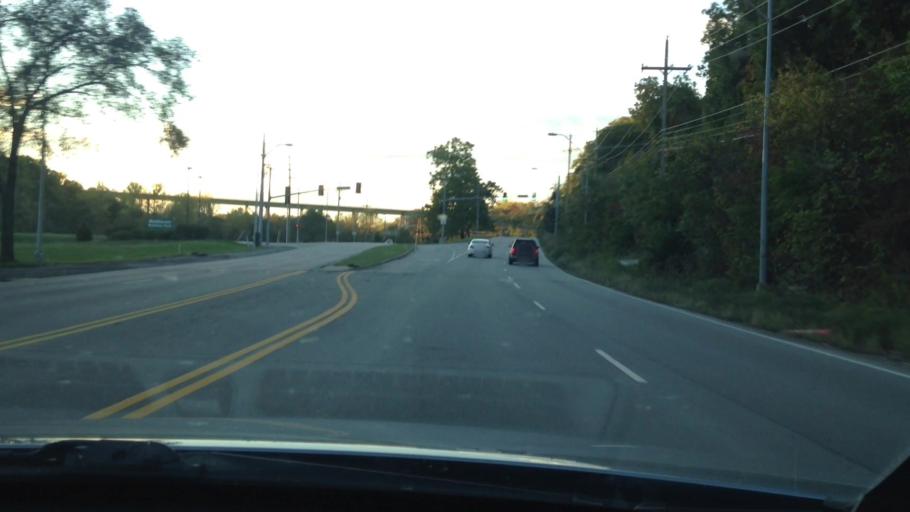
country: US
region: Missouri
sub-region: Jackson County
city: Raytown
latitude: 39.0131
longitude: -94.5096
